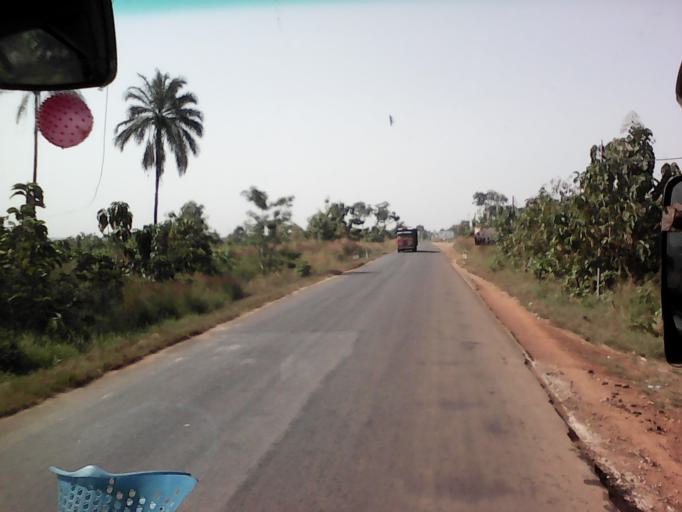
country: TG
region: Centrale
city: Sokode
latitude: 8.9510
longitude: 1.1323
